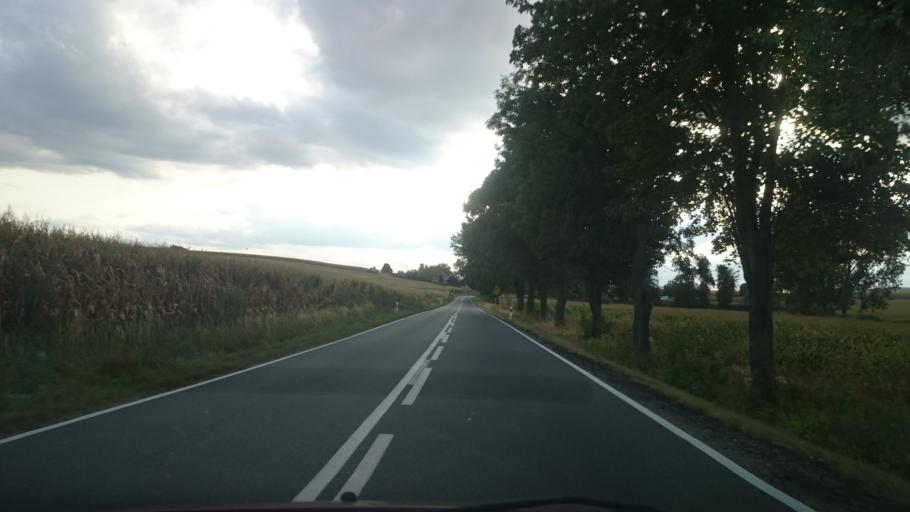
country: PL
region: Lower Silesian Voivodeship
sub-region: Powiat zabkowicki
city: Ziebice
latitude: 50.5881
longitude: 16.9697
